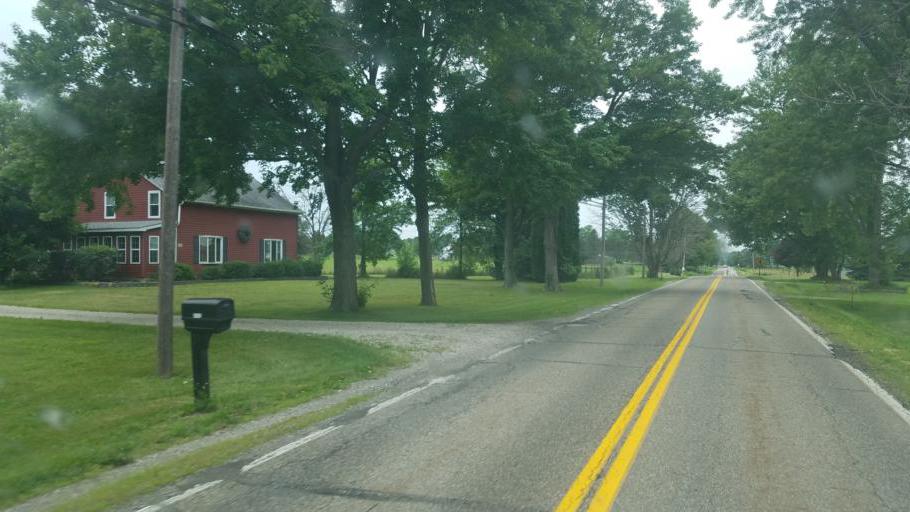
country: US
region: Ohio
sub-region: Portage County
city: Ravenna
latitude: 41.0991
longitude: -81.1668
